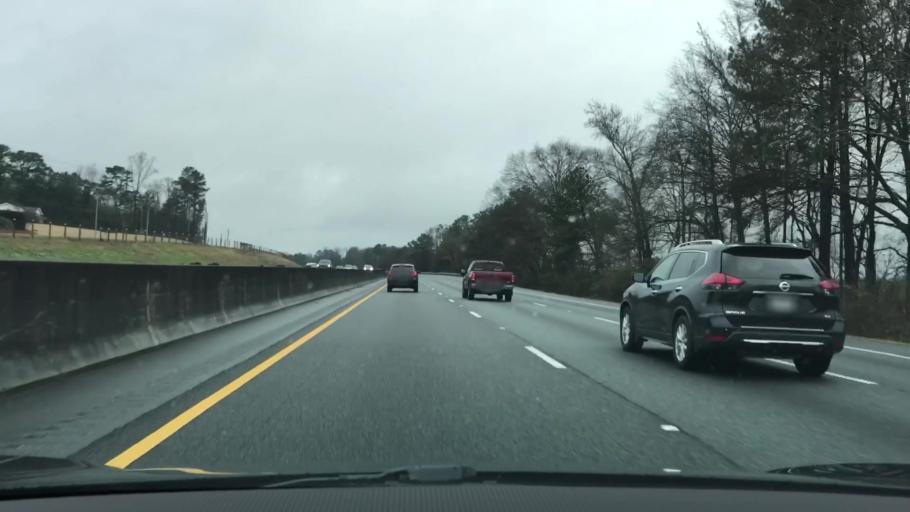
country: US
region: Georgia
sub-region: Newton County
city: Porterdale
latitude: 33.6259
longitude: -83.9410
